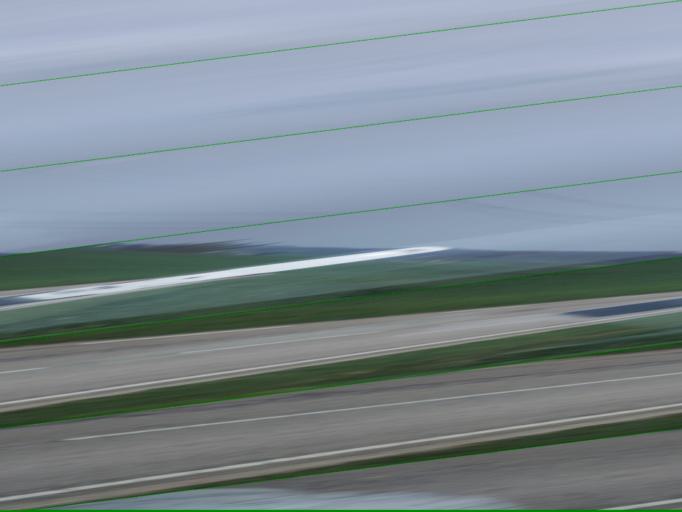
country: FR
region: Ile-de-France
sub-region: Departement des Yvelines
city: Houdan
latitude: 48.8079
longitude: 1.5992
